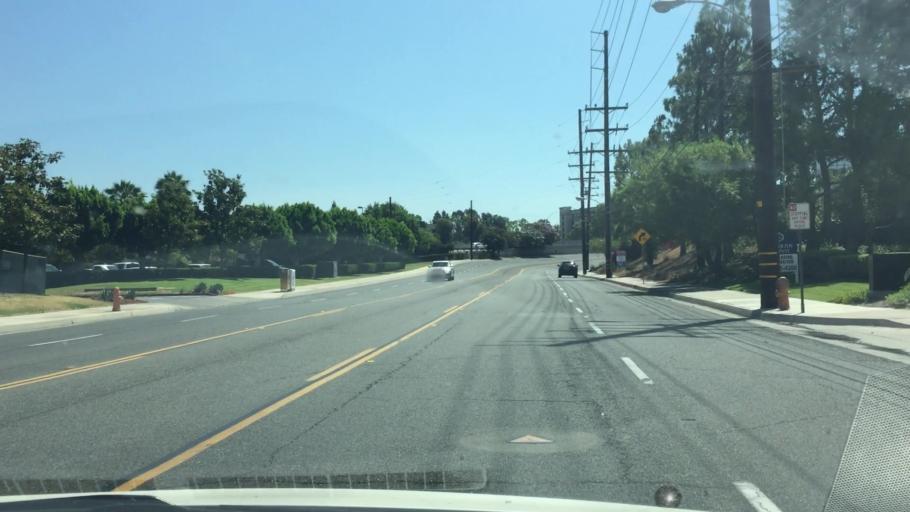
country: US
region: California
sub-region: Orange County
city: Laguna Hills
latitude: 33.6272
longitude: -117.7219
